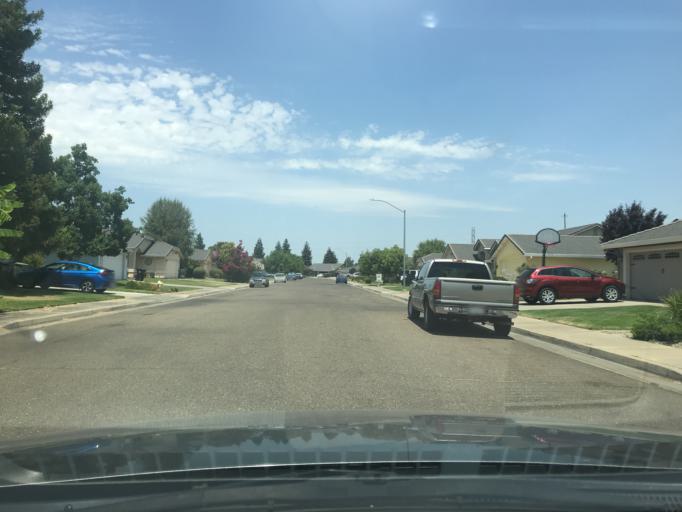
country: US
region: California
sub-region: Merced County
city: Atwater
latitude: 37.3648
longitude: -120.5914
